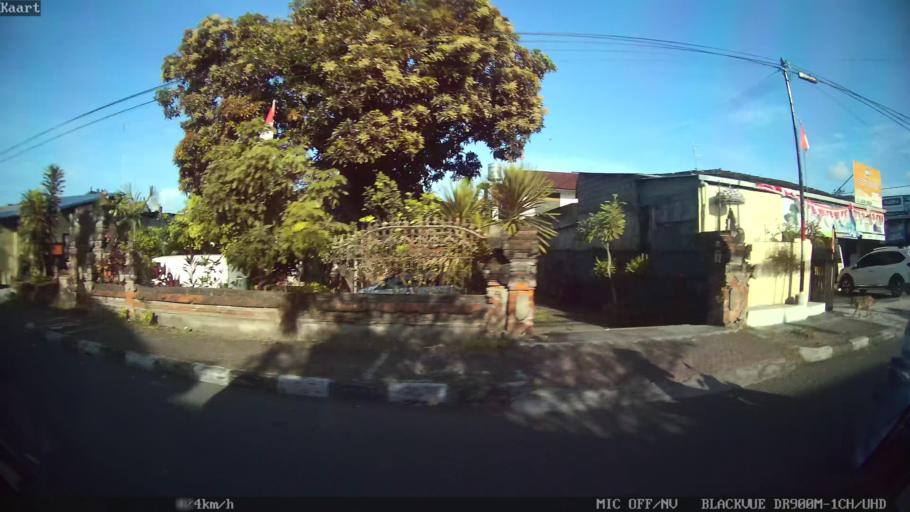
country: ID
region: Bali
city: Denpasar
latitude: -8.6434
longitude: 115.2207
